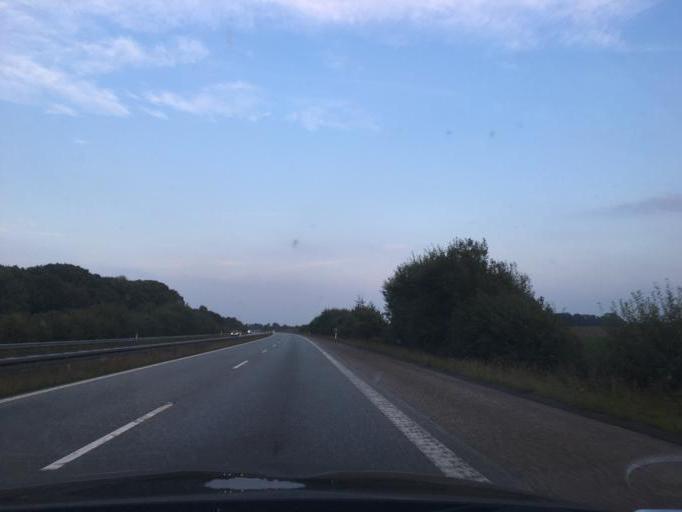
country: DK
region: South Denmark
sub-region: Vejen Kommune
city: Vejen
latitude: 55.4967
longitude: 9.0881
